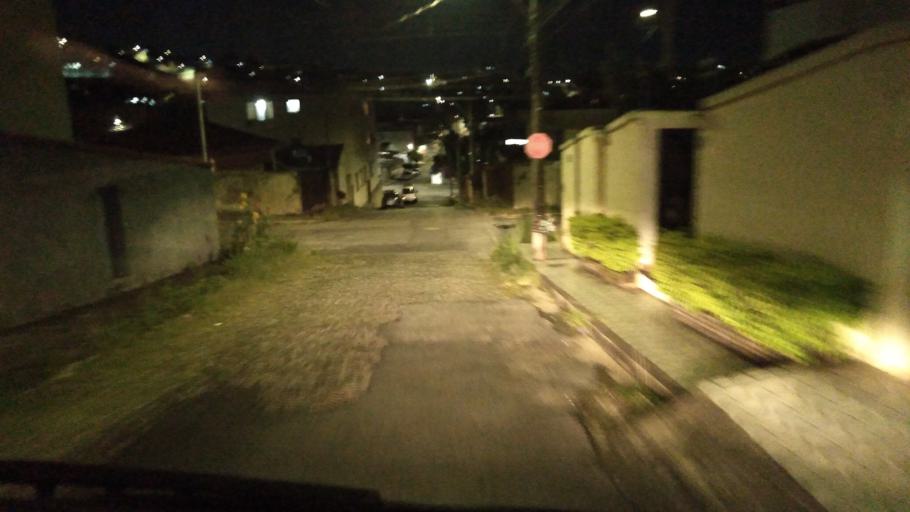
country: BR
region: Minas Gerais
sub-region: Belo Horizonte
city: Belo Horizonte
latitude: -19.8911
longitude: -43.9389
